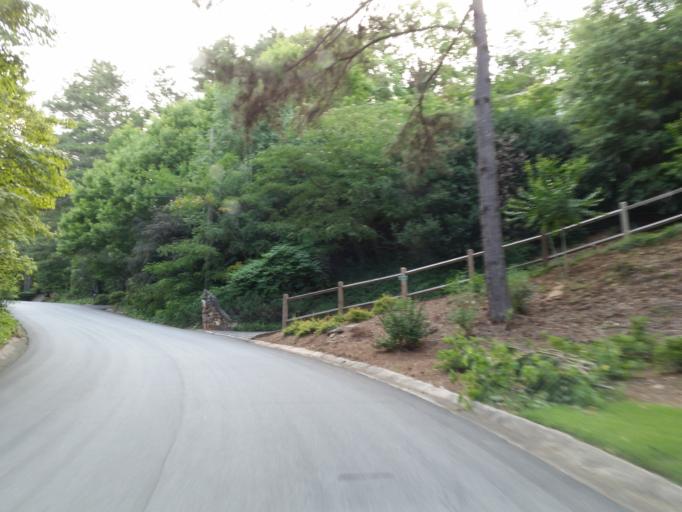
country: US
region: Georgia
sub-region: Cobb County
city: Vinings
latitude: 33.8684
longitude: -84.4570
